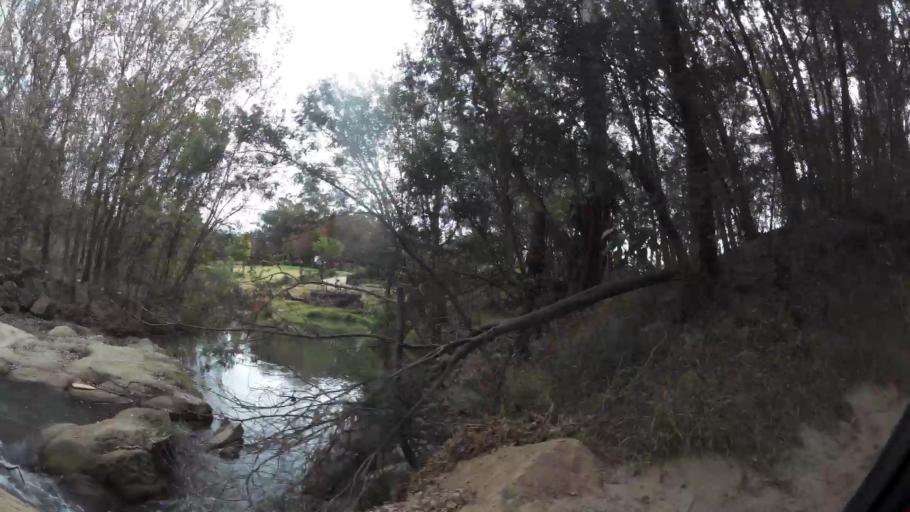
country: ZA
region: Gauteng
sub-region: West Rand District Municipality
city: Muldersdriseloop
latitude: -26.0689
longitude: 27.8822
